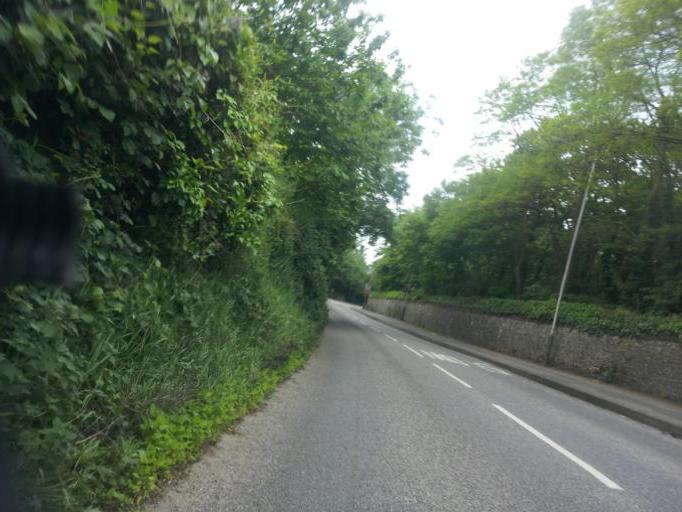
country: GB
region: England
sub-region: Kent
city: Larkfield
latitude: 51.2963
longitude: 0.4382
